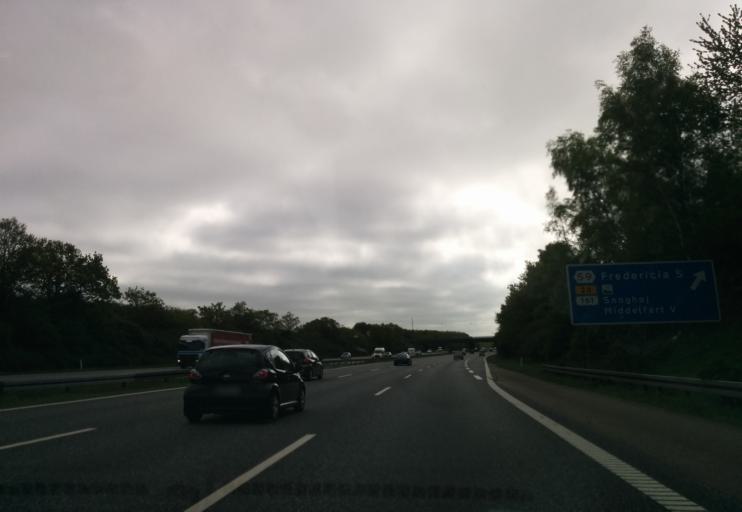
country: DK
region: South Denmark
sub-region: Fredericia Kommune
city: Snoghoj
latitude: 55.5347
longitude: 9.7108
